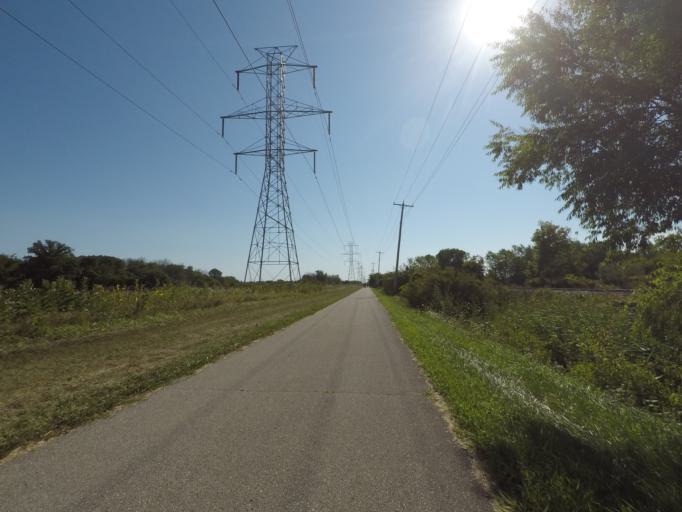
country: US
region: Wisconsin
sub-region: Waukesha County
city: New Berlin
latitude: 43.0101
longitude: -88.1551
